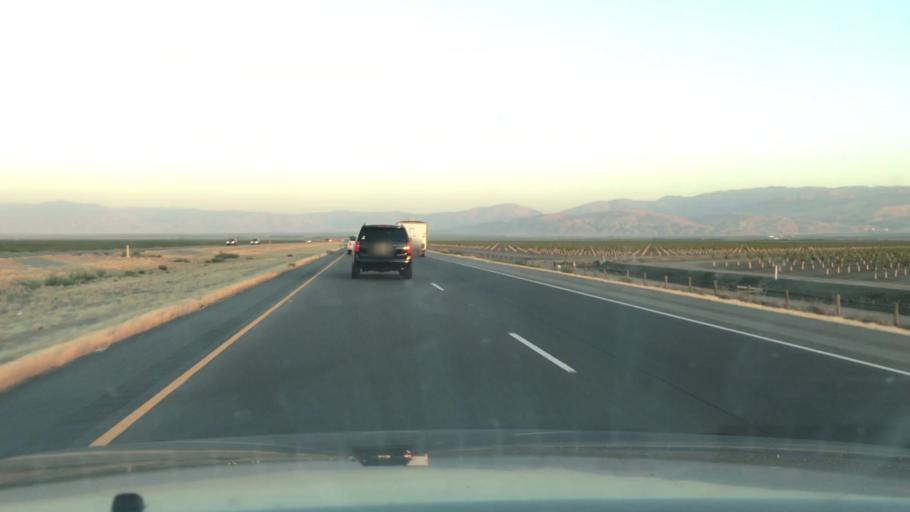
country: US
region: California
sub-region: Kern County
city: Greenfield
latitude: 35.1449
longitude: -119.0925
